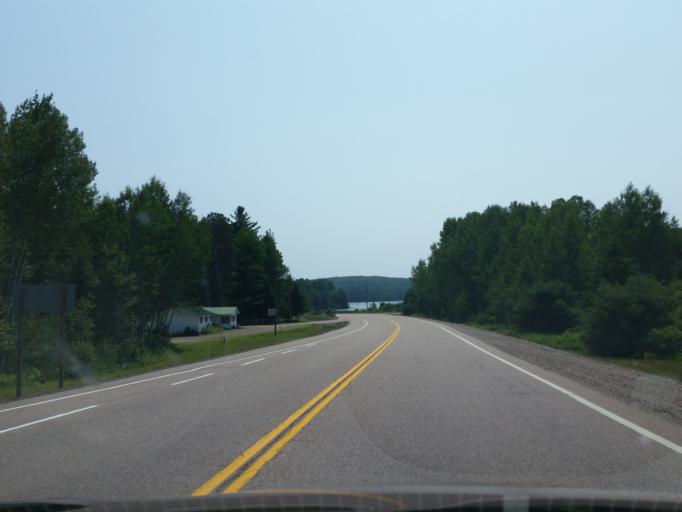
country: CA
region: Ontario
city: Deep River
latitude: 46.1704
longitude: -77.8210
